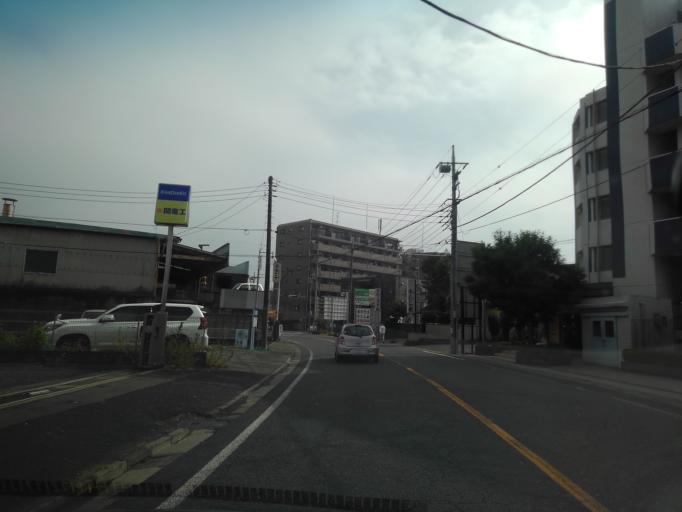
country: JP
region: Saitama
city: Tokorozawa
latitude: 35.7945
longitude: 139.4590
